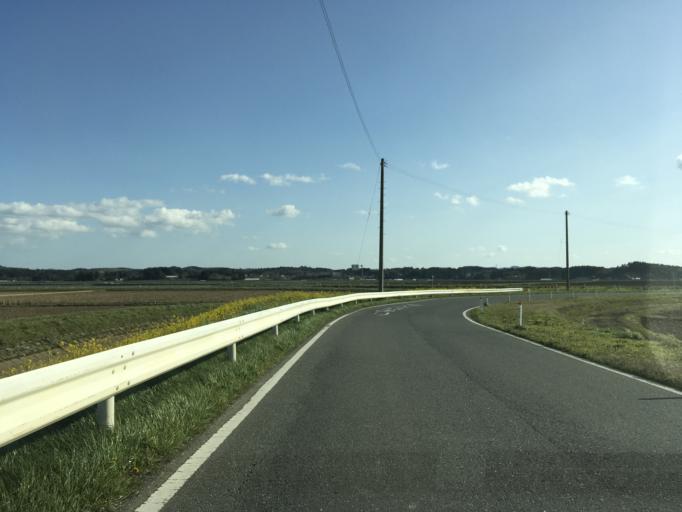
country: JP
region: Miyagi
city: Wakuya
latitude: 38.6560
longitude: 141.2381
